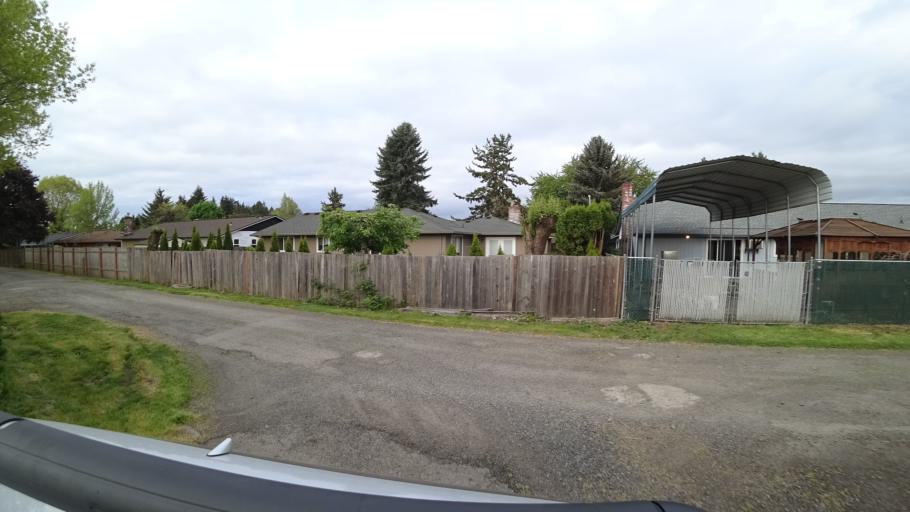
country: US
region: Oregon
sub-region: Washington County
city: Hillsboro
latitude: 45.5086
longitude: -122.9291
